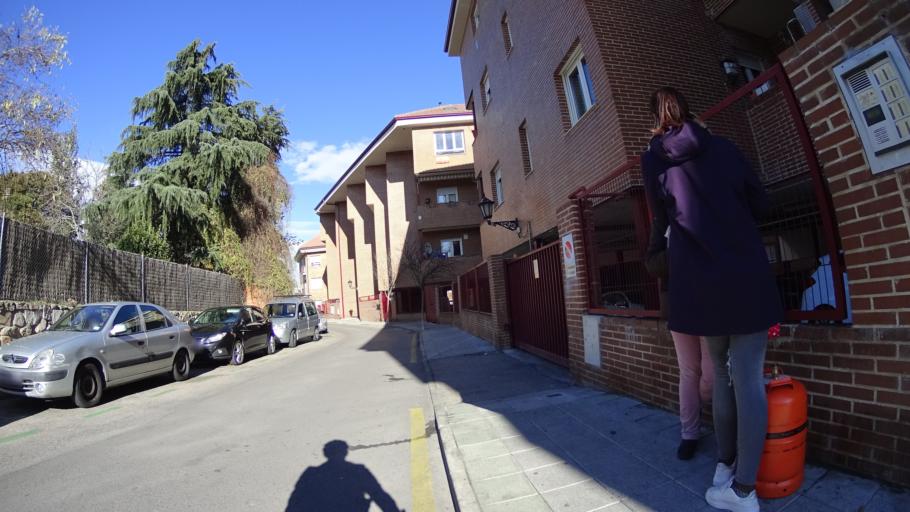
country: ES
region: Madrid
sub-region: Provincia de Madrid
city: Galapagar
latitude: 40.5761
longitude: -4.0082
